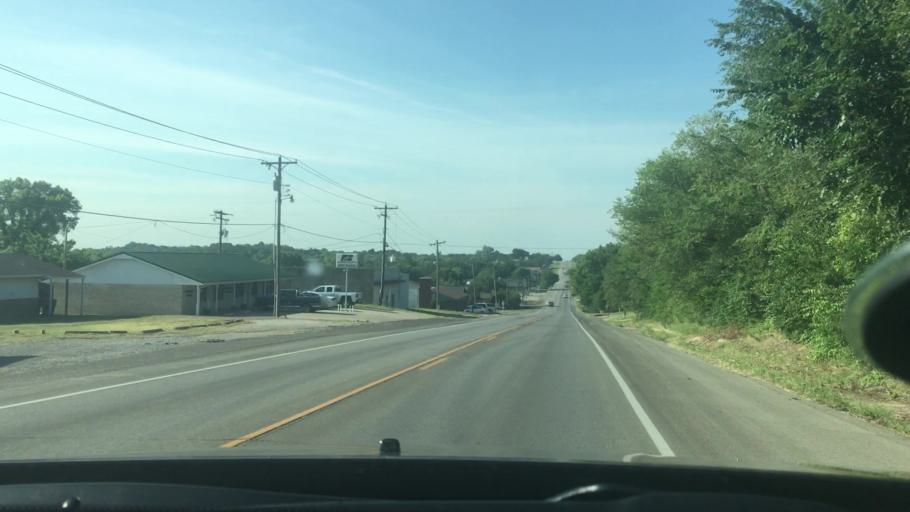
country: US
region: Oklahoma
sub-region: Garvin County
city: Pauls Valley
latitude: 34.7252
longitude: -97.2130
